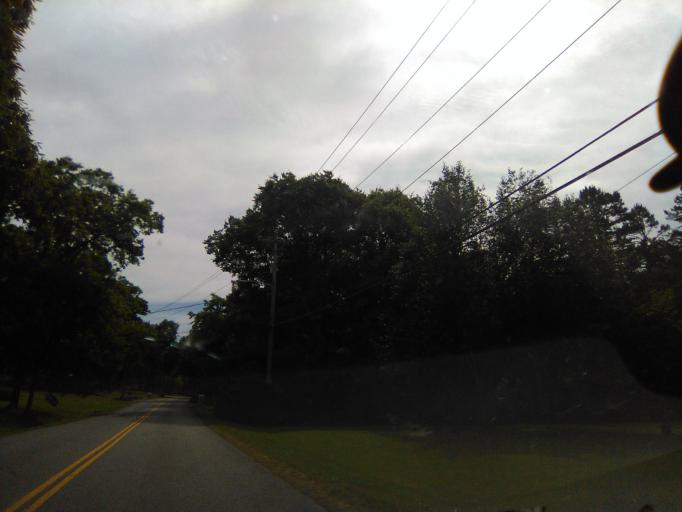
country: US
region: Tennessee
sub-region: Davidson County
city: Belle Meade
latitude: 36.1028
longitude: -86.9008
